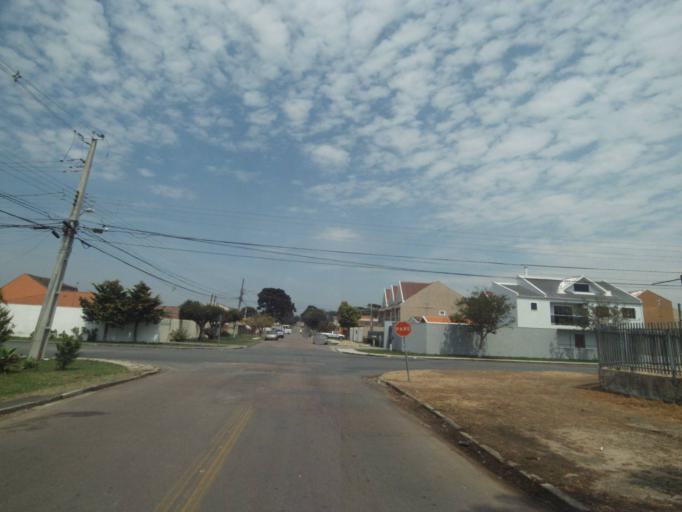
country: BR
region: Parana
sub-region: Pinhais
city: Pinhais
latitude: -25.4245
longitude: -49.2004
